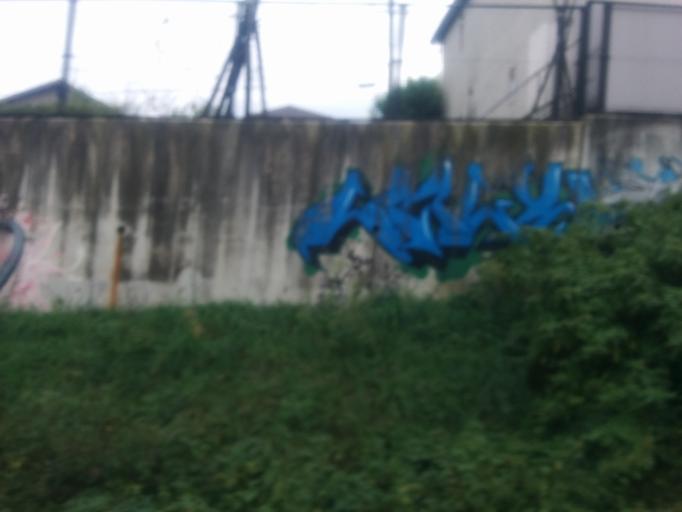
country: JP
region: Kyoto
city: Uji
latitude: 34.9451
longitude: 135.7741
